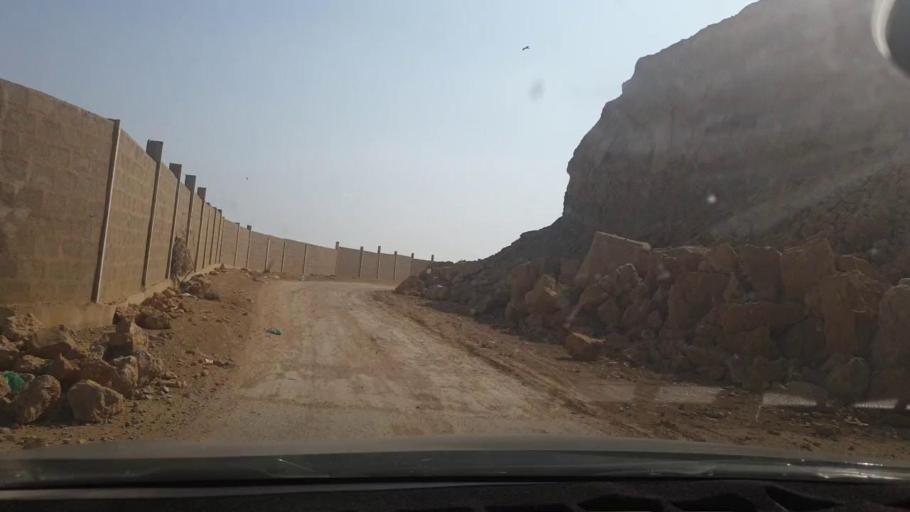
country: PK
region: Sindh
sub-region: Karachi District
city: Karachi
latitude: 24.9674
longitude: 66.9980
